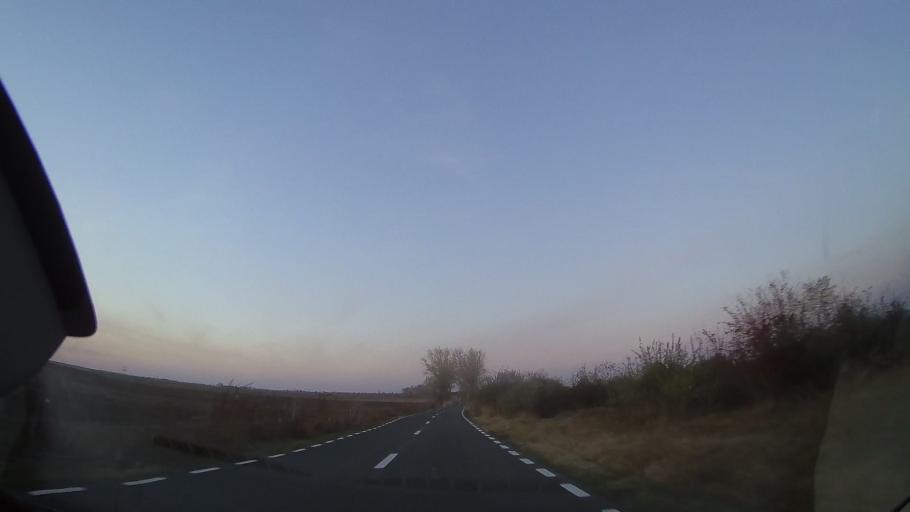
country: RO
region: Constanta
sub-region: Comuna Cobadin
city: Cobadin
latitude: 44.0371
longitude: 28.2587
